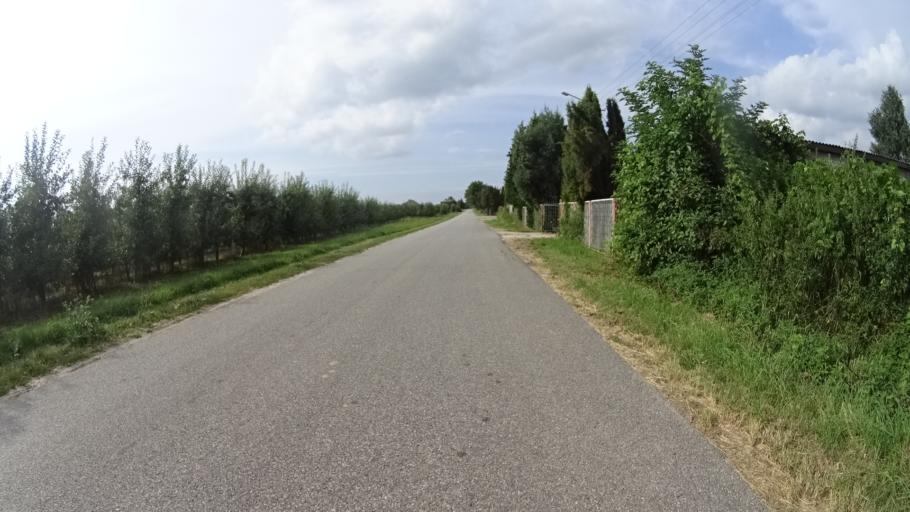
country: PL
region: Masovian Voivodeship
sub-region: Powiat grojecki
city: Goszczyn
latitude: 51.7029
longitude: 20.8458
